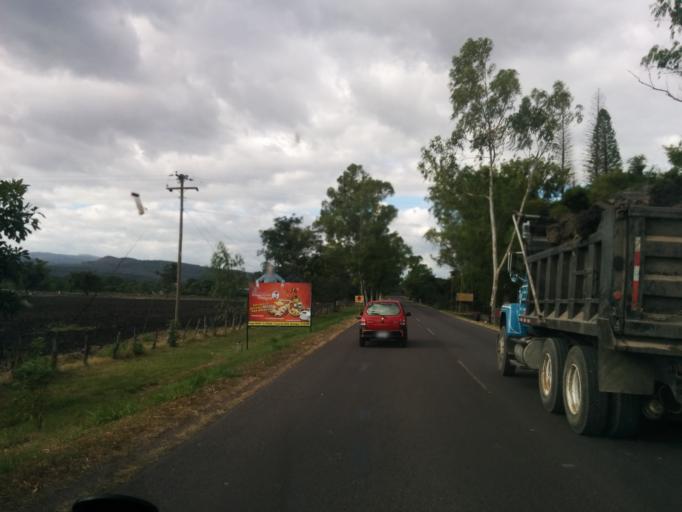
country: NI
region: Esteli
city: Esteli
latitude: 13.1478
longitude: -86.3688
